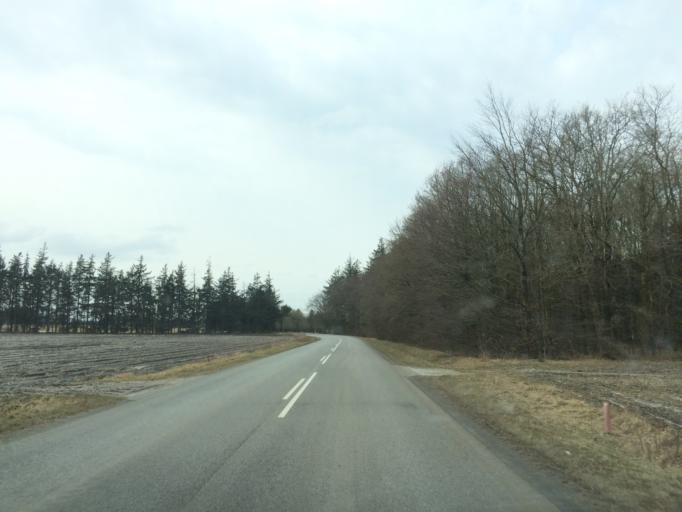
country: DK
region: Central Jutland
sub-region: Ringkobing-Skjern Kommune
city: Tarm
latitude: 55.8465
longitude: 8.4807
